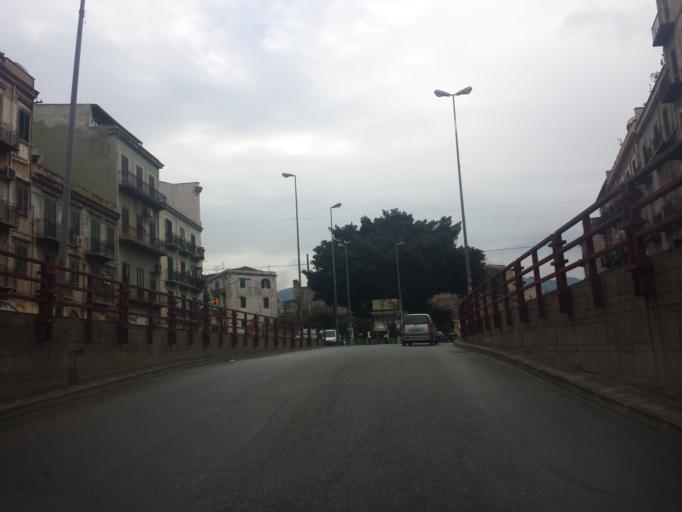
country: IT
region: Sicily
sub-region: Palermo
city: Palermo
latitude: 38.1181
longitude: 13.3510
